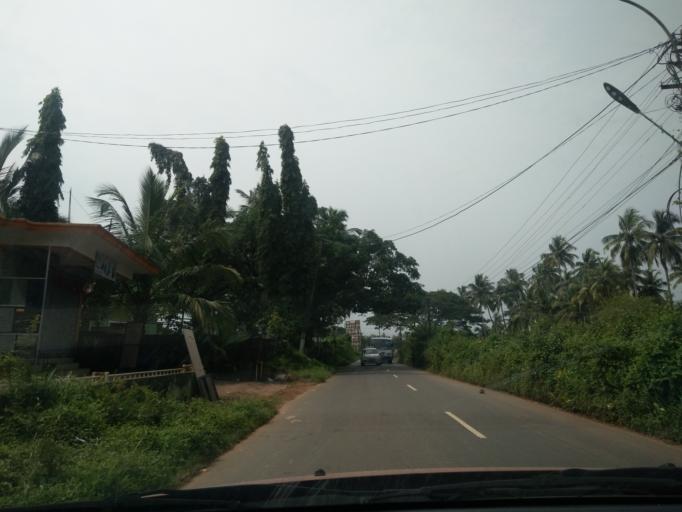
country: IN
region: Goa
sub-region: North Goa
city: Goa Velha
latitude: 15.4413
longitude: 73.8788
